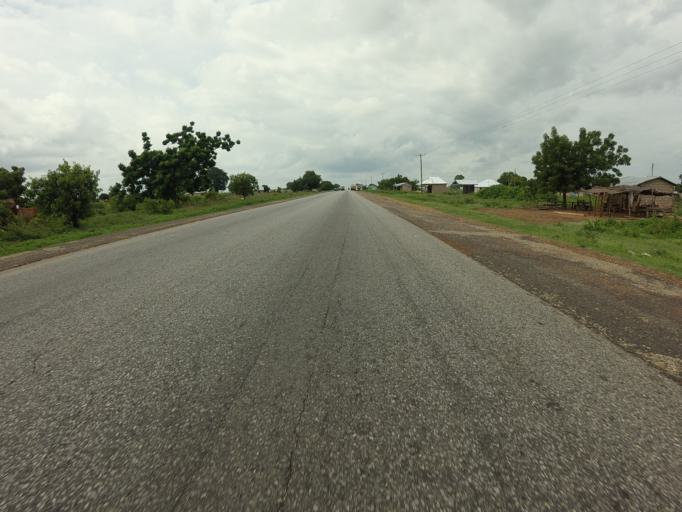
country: GH
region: Brong-Ahafo
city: Kintampo
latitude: 8.7340
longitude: -1.4736
